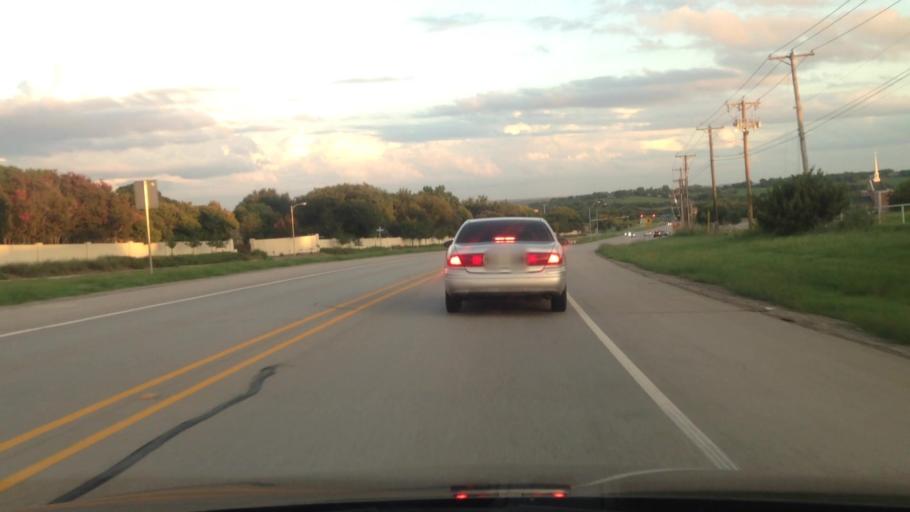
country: US
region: Texas
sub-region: Tarrant County
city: Benbrook
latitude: 32.6689
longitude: -97.4909
